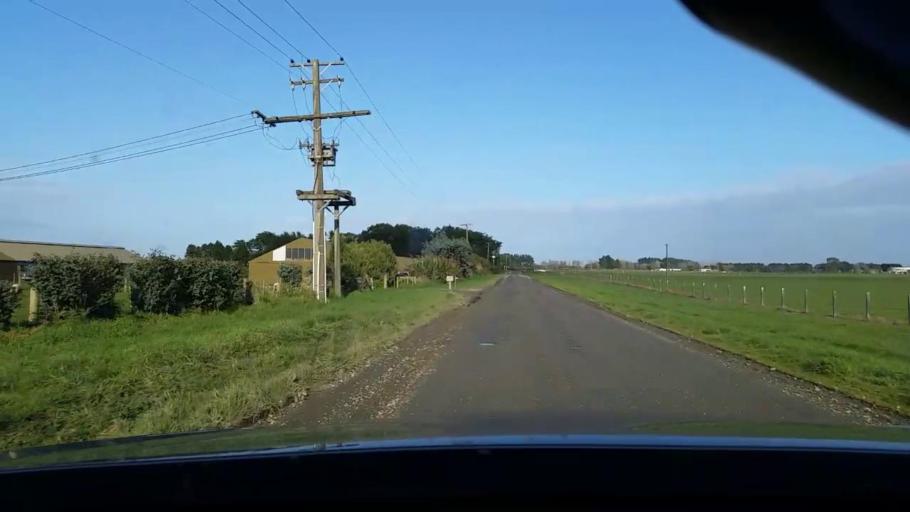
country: NZ
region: Southland
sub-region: Invercargill City
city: Invercargill
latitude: -46.3062
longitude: 168.3034
